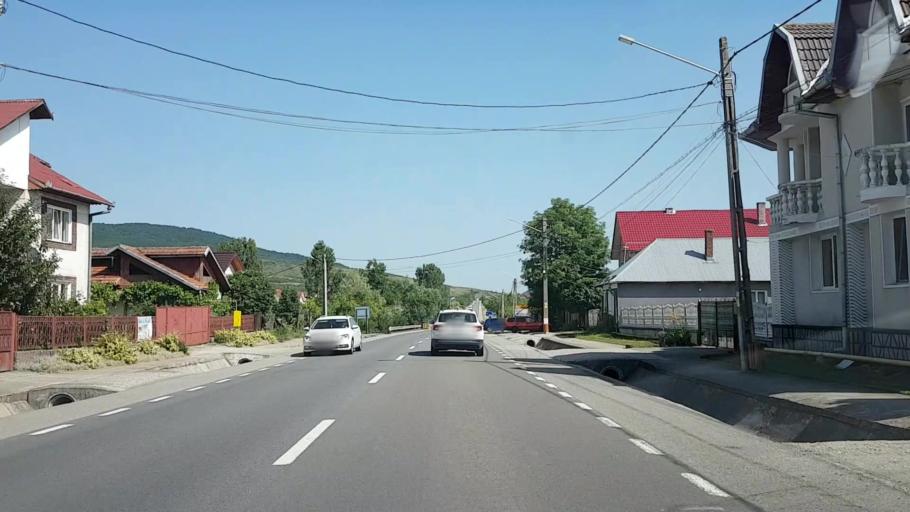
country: RO
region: Bistrita-Nasaud
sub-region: Comuna Sieu-Magherus
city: Sieu-Magherus
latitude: 47.0880
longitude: 24.3795
